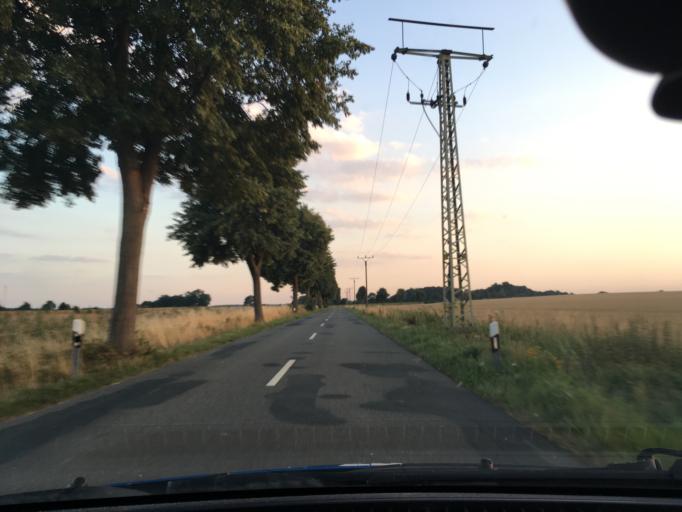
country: DE
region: Lower Saxony
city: Natendorf
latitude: 53.1048
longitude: 10.4536
